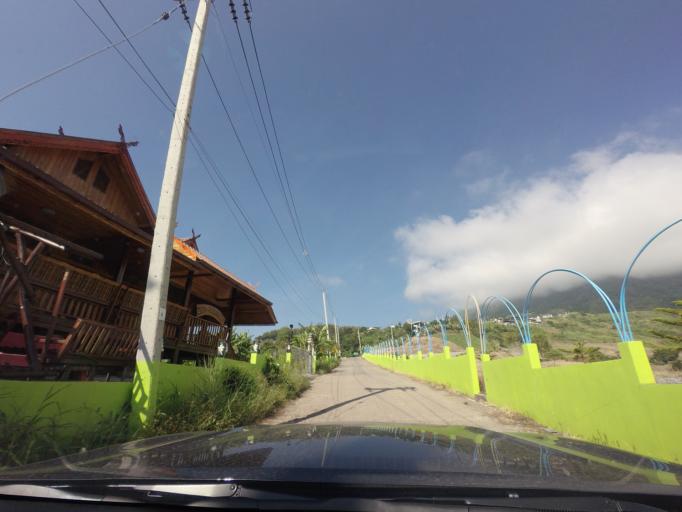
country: TH
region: Phetchabun
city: Khao Kho
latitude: 16.7922
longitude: 101.0478
